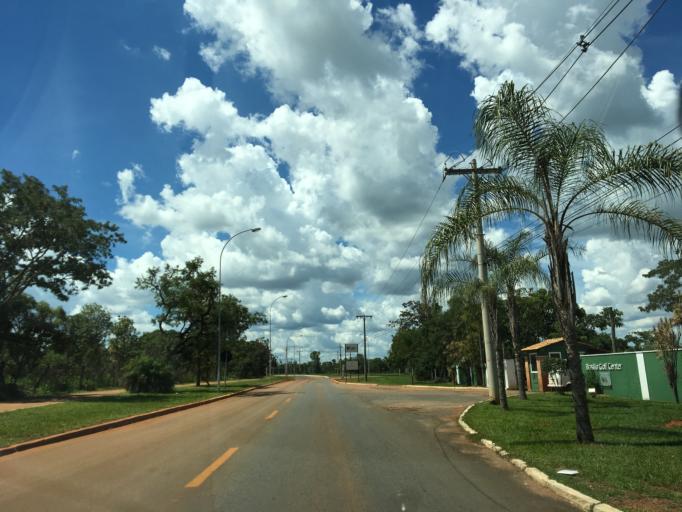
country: BR
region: Federal District
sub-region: Brasilia
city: Brasilia
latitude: -15.8090
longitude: -47.8375
